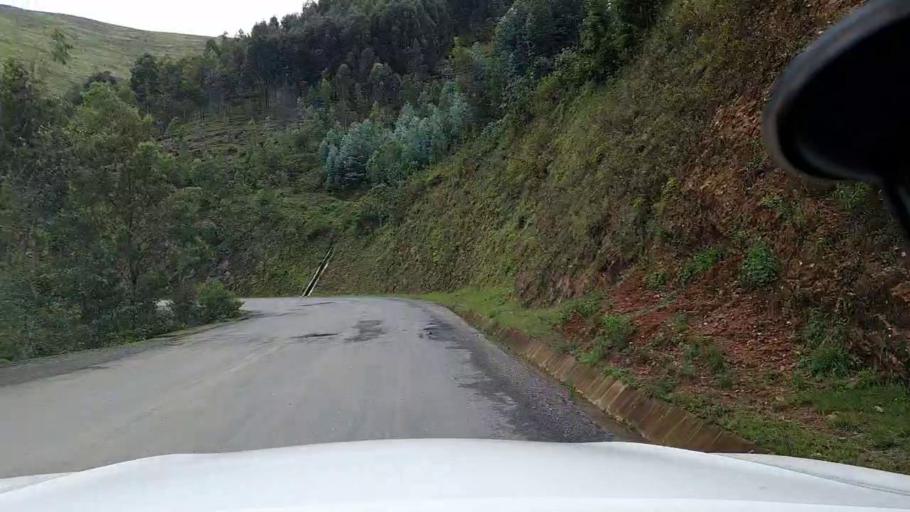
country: RW
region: Southern Province
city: Gitarama
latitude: -2.0614
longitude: 29.5618
